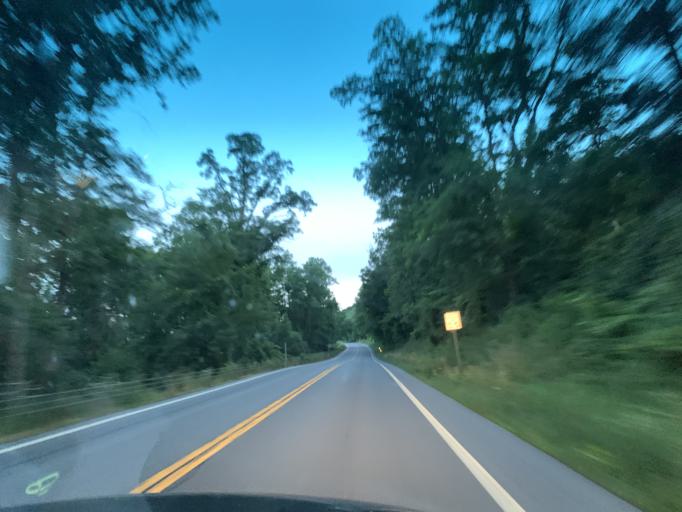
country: US
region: New York
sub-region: Chenango County
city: New Berlin
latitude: 42.6759
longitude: -75.3309
